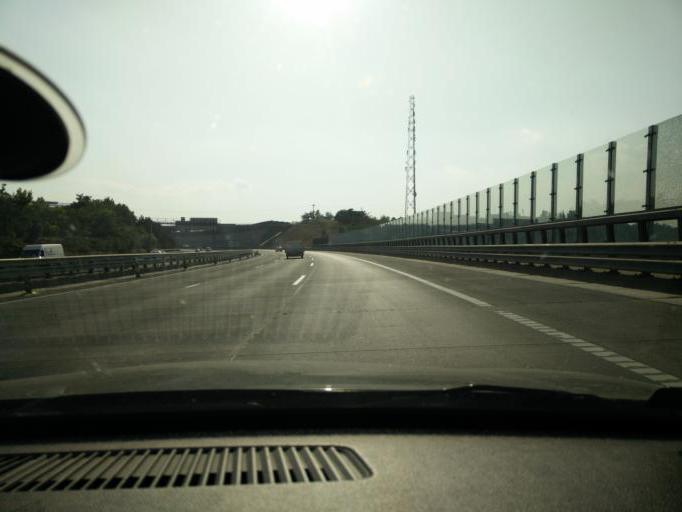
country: HU
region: Pest
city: Diosd
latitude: 47.4209
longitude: 18.9446
